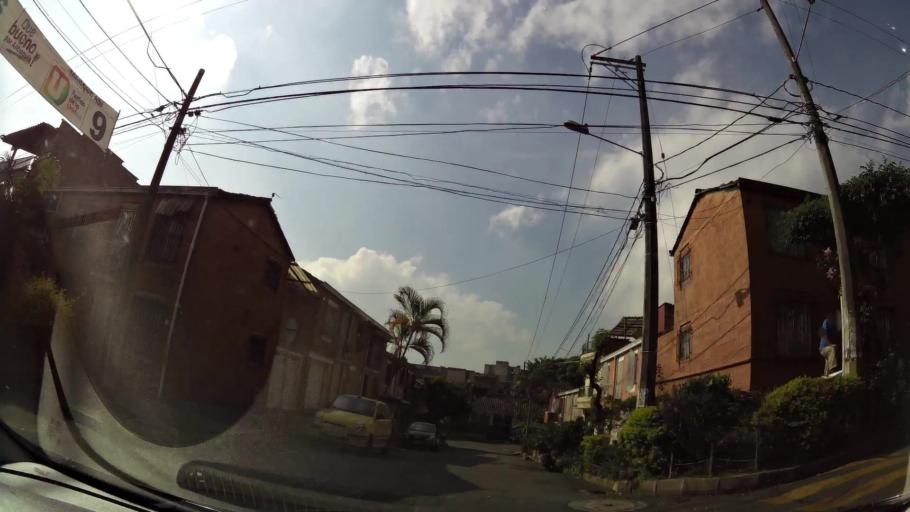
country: CO
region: Antioquia
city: La Estrella
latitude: 6.1716
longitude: -75.6384
